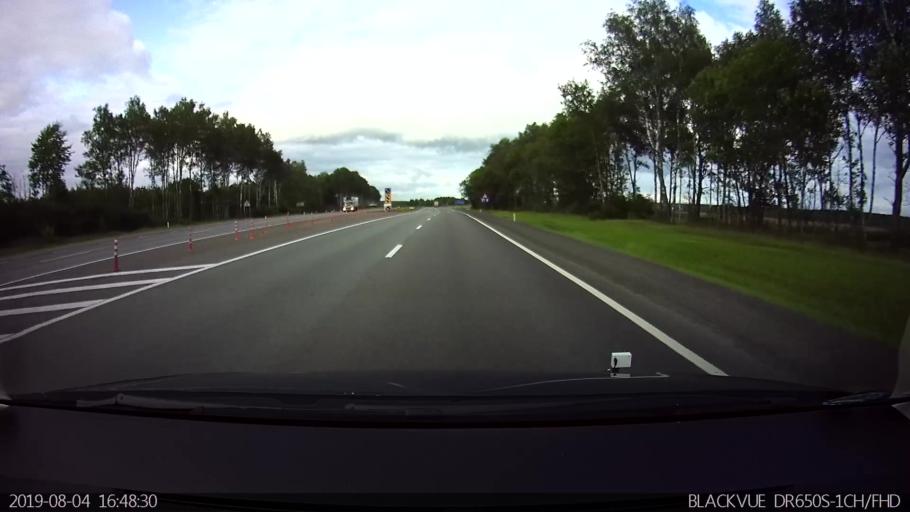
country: RU
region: Smolensk
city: Vyaz'ma
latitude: 55.2024
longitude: 34.1358
